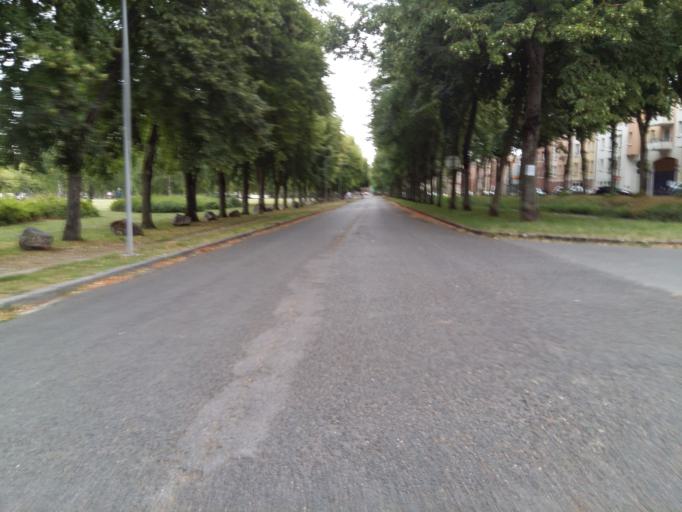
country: FR
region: Picardie
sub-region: Departement de la Somme
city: Amiens
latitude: 49.8977
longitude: 2.2780
